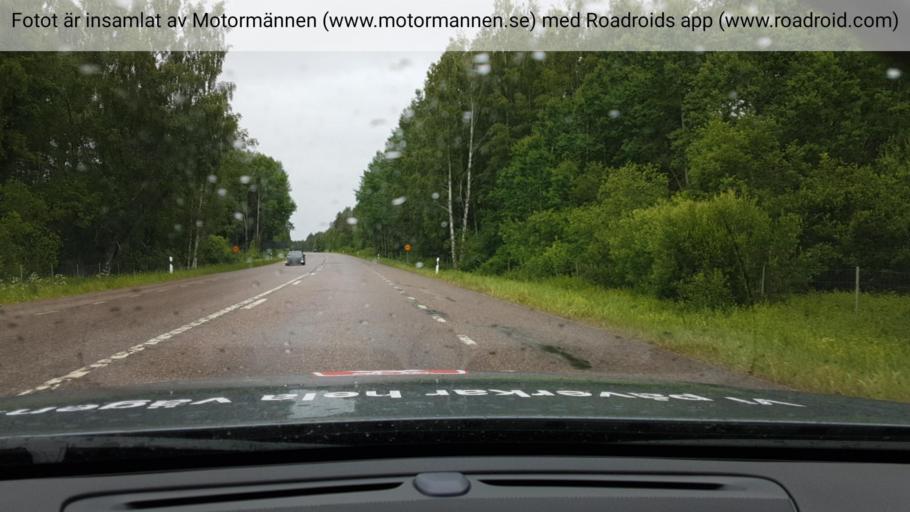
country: SE
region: Uppsala
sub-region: Alvkarleby Kommun
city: AElvkarleby
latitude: 60.5863
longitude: 17.4650
